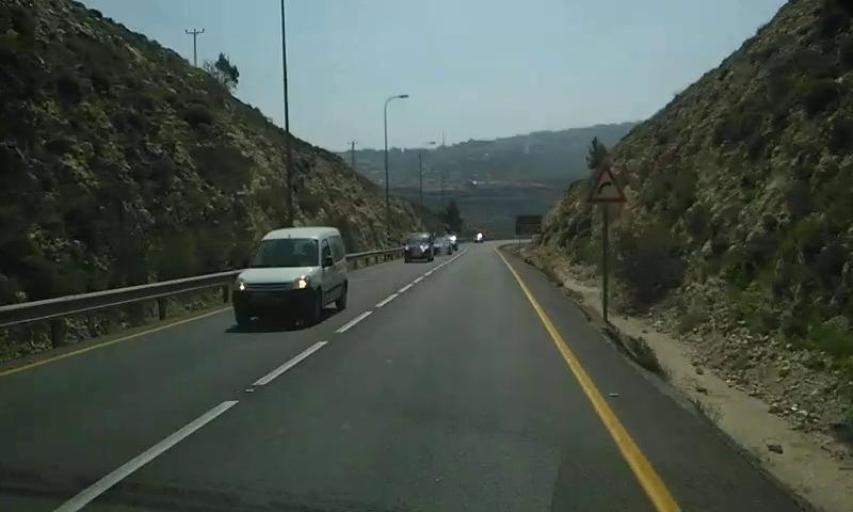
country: PS
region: West Bank
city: Mikhmas
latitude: 31.8748
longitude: 35.2646
